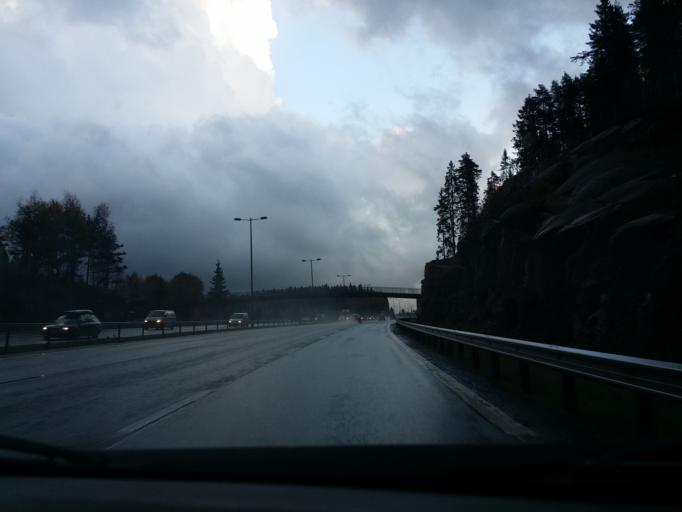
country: NO
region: Buskerud
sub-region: Lier
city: Tranby
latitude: 59.8069
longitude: 10.2804
